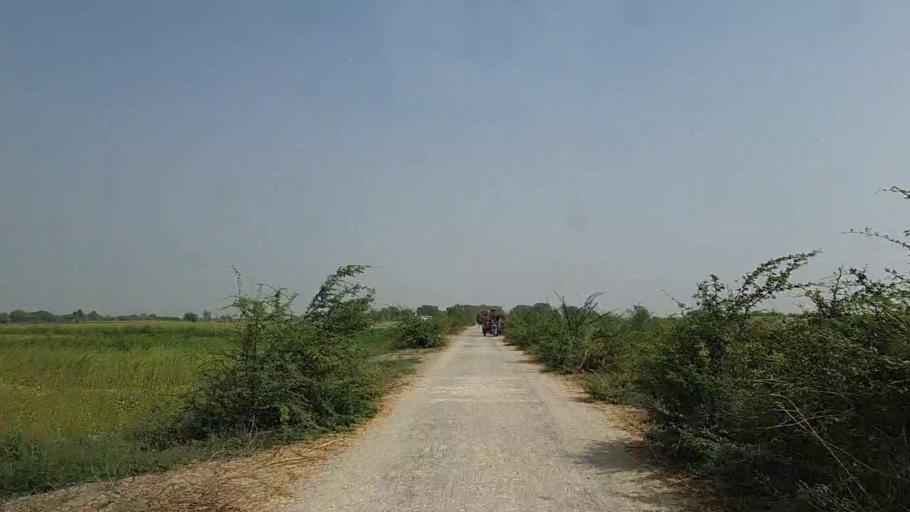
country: PK
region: Sindh
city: Naukot
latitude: 24.7836
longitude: 69.3578
